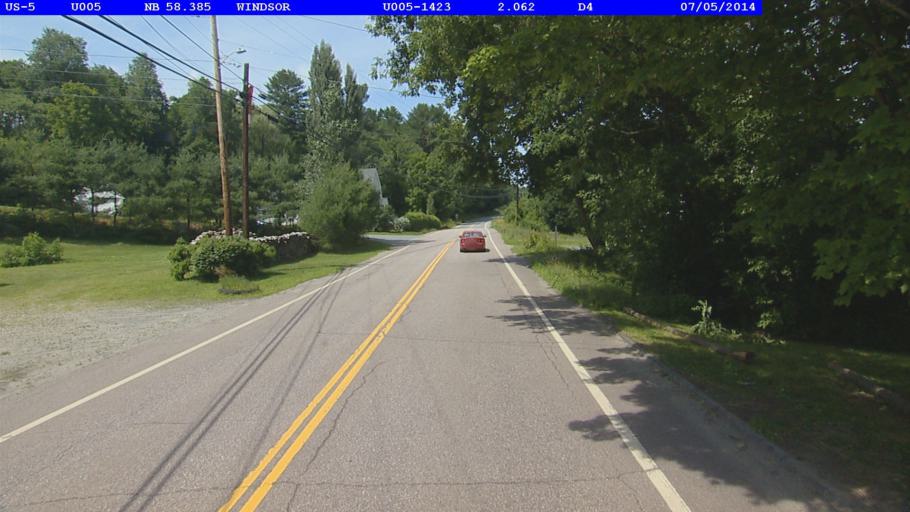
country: US
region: Vermont
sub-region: Windsor County
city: Windsor
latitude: 43.4579
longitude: -72.3942
